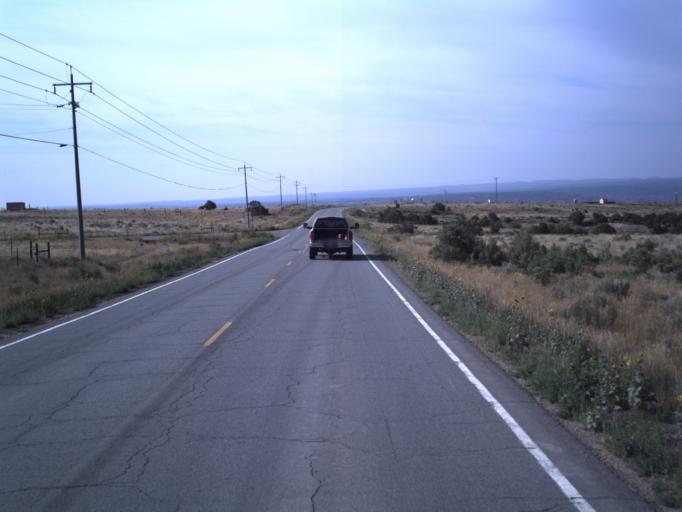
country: US
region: Utah
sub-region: Duchesne County
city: Duchesne
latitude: 40.2041
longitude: -110.3893
